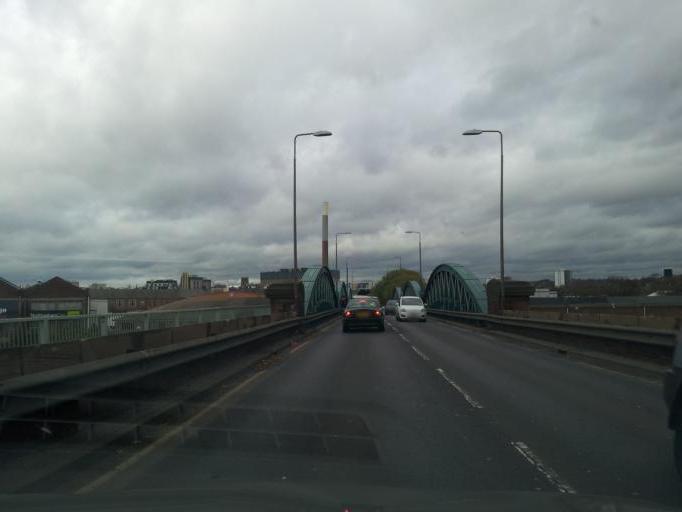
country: GB
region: England
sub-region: Nottinghamshire
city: West Bridgford
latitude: 52.9423
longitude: -1.1311
